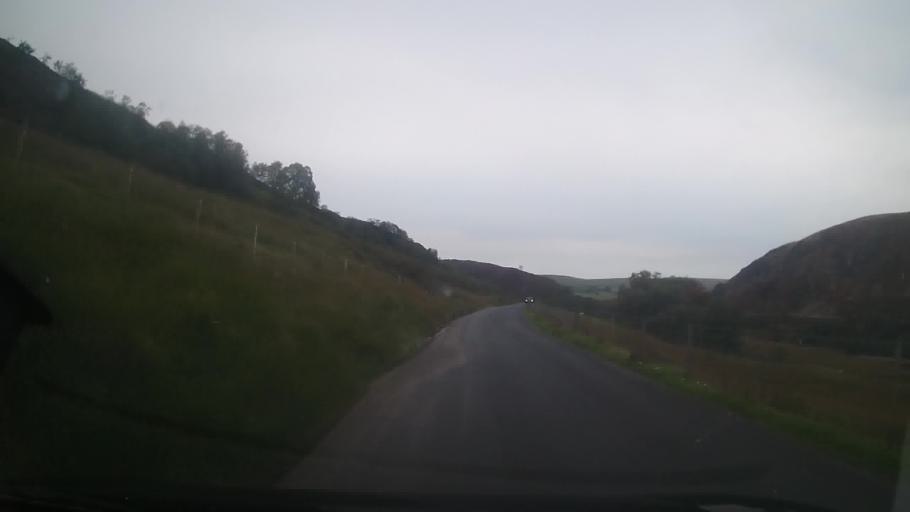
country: GB
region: Wales
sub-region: Sir Powys
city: Rhayader
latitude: 52.2978
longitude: -3.6209
